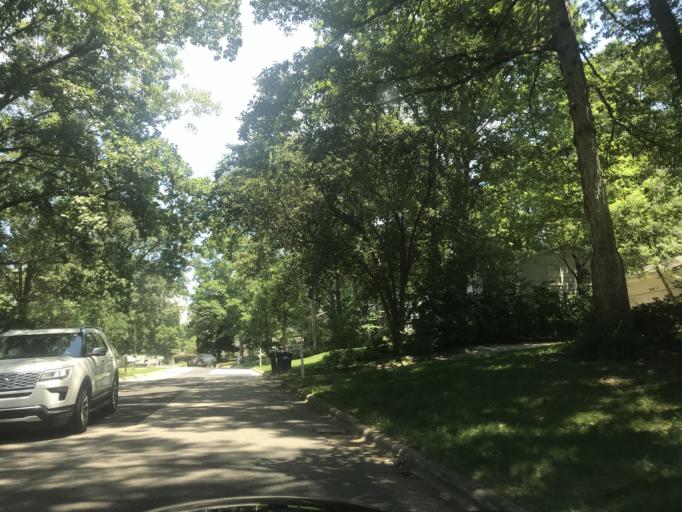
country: US
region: North Carolina
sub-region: Wake County
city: West Raleigh
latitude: 35.8885
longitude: -78.6218
